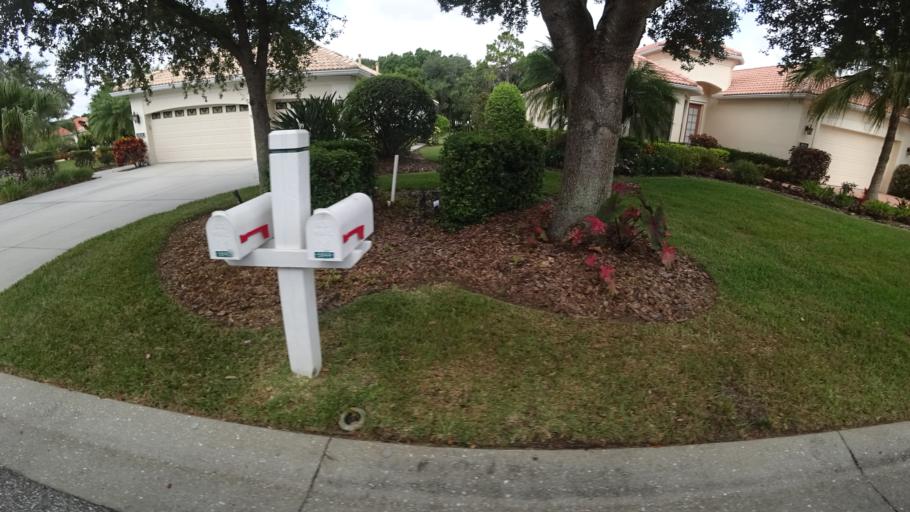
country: US
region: Florida
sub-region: Sarasota County
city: Desoto Lakes
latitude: 27.4373
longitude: -82.4663
